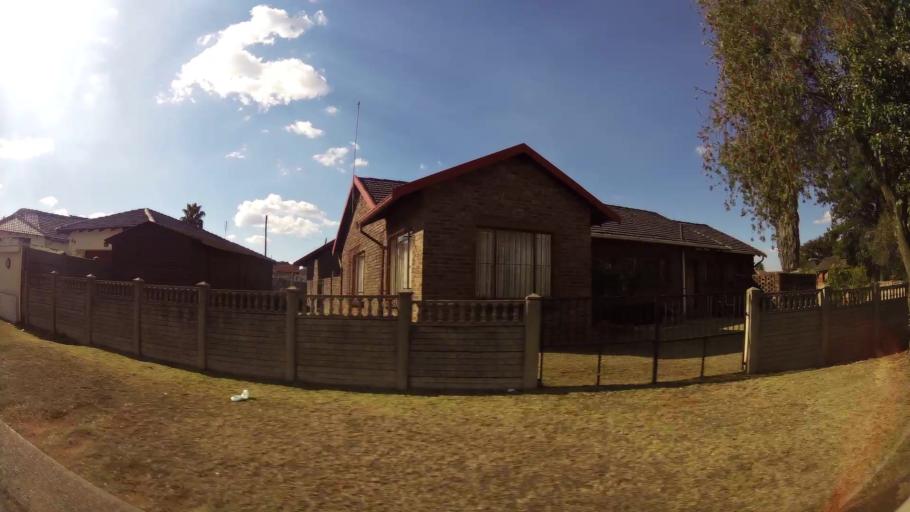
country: ZA
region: Mpumalanga
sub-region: Nkangala District Municipality
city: Witbank
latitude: -25.9171
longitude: 29.2237
